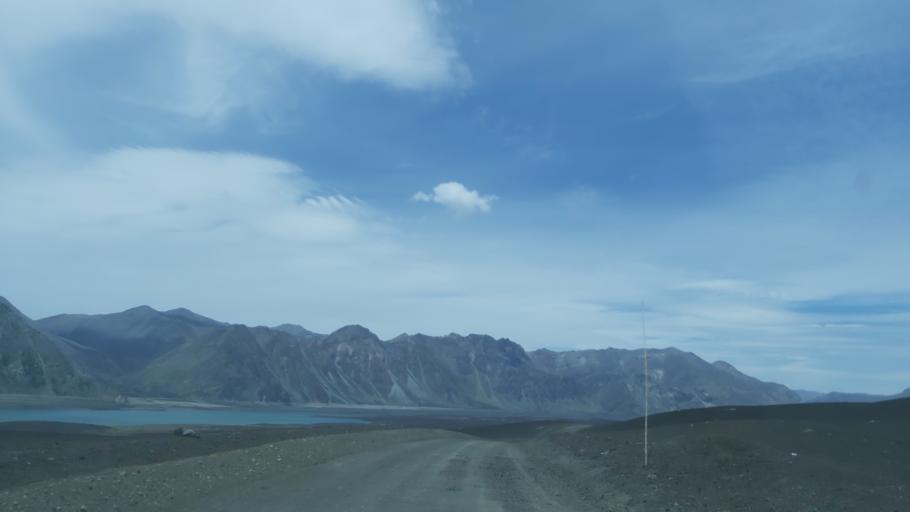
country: AR
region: Neuquen
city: Andacollo
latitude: -37.4143
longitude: -71.2912
